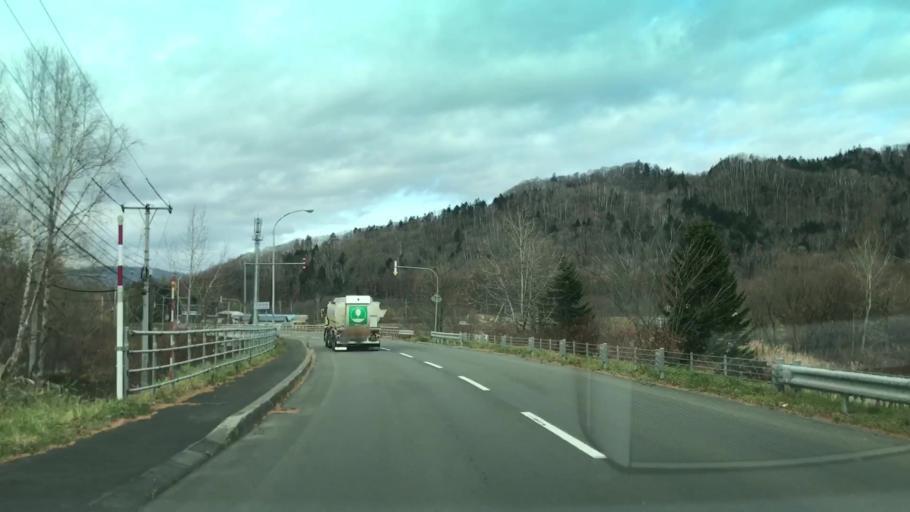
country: JP
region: Hokkaido
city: Shimo-furano
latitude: 42.9488
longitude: 142.4424
